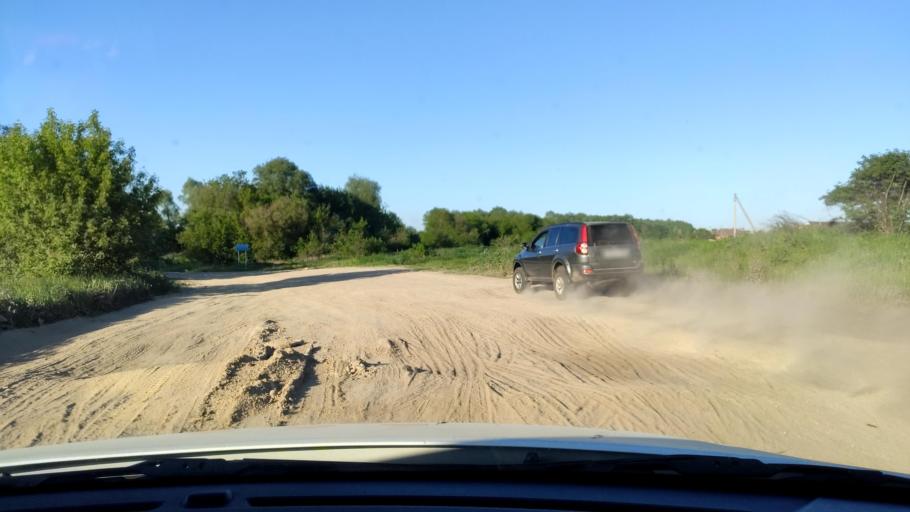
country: RU
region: Tatarstan
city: Pestretsy
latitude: 55.6181
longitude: 49.4895
